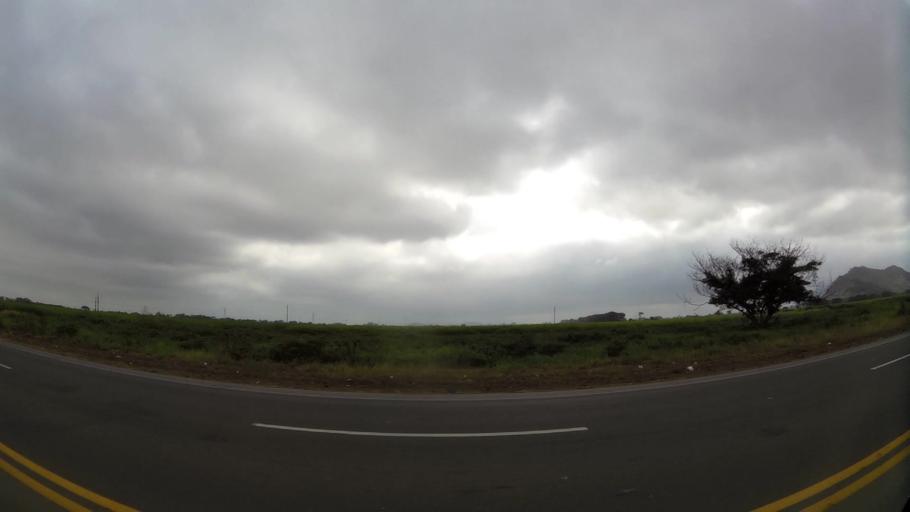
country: EC
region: Guayas
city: Coronel Marcelino Mariduena
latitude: -2.3626
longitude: -79.6330
